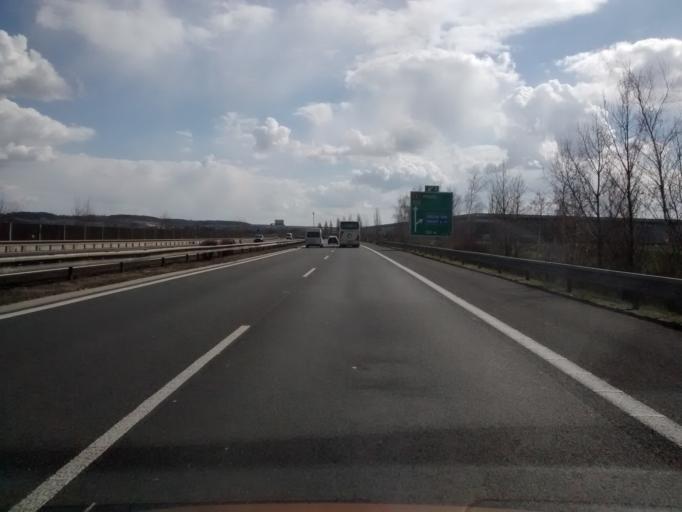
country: CZ
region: Central Bohemia
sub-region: Okres Melnik
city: Veltrusy
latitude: 50.2558
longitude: 14.3704
